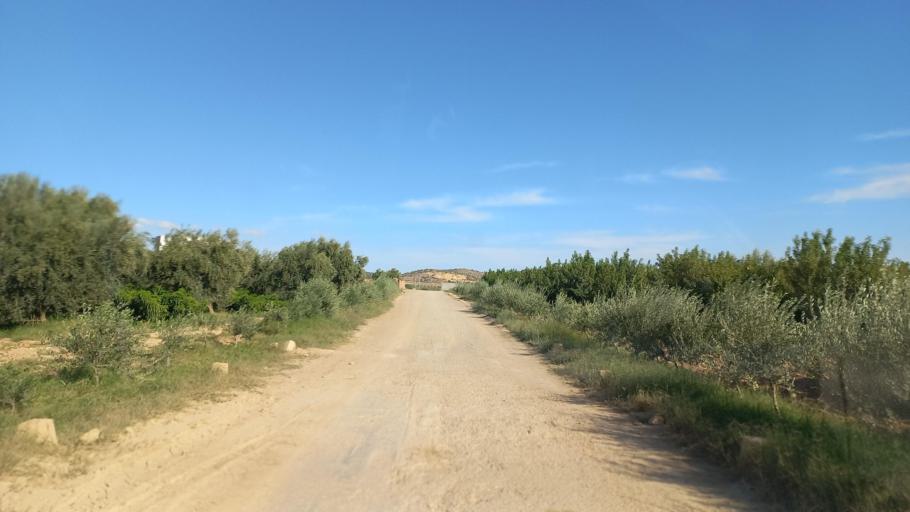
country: TN
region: Al Qasrayn
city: Sbiba
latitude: 35.2968
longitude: 9.0987
